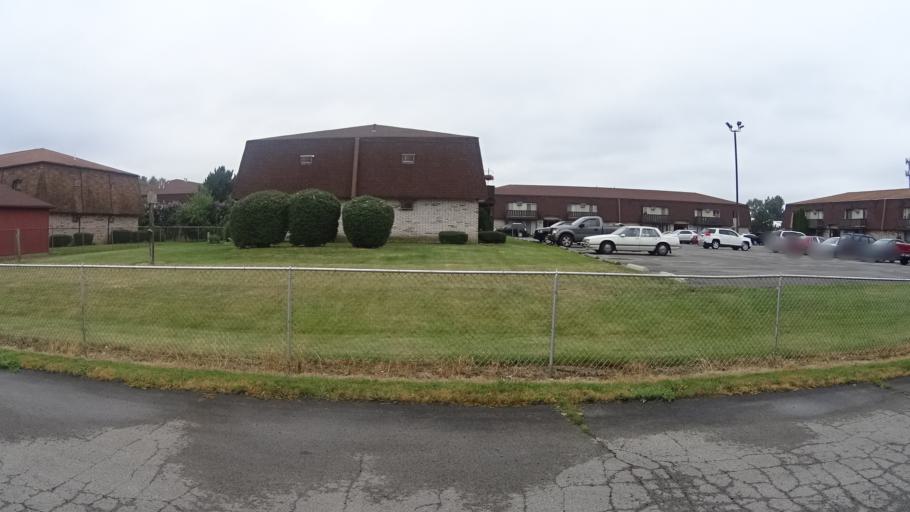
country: US
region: Ohio
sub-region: Erie County
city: Sandusky
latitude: 41.4382
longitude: -82.6672
